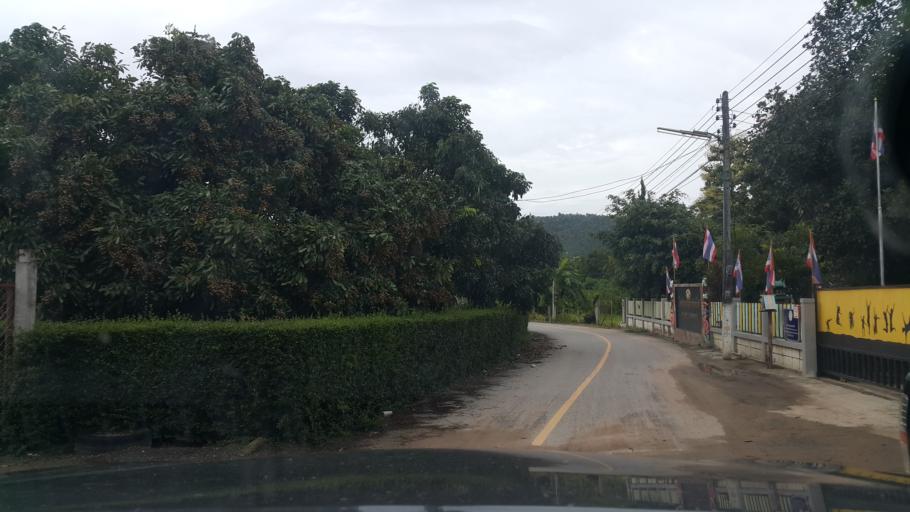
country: TH
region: Chiang Mai
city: Mae On
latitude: 18.8373
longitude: 99.1854
